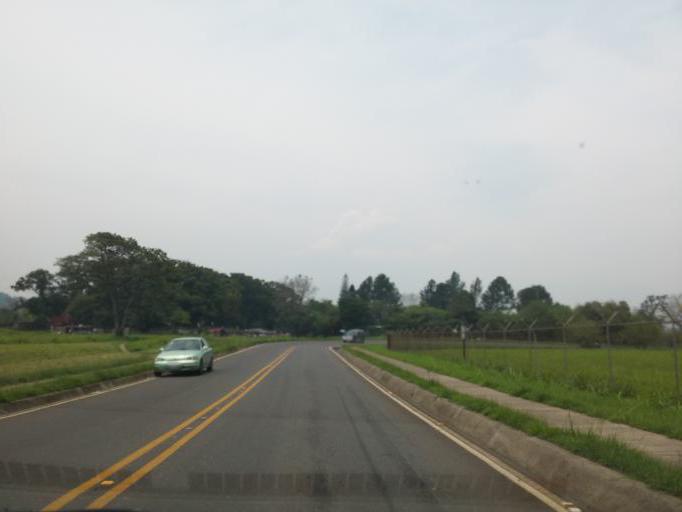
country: CR
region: Heredia
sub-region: Canton de Belen
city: San Antonio
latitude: 9.9974
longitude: -84.1946
